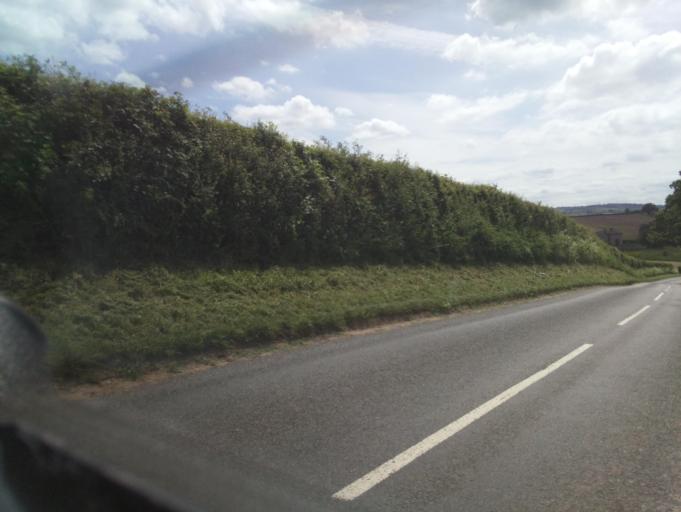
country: GB
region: England
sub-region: Herefordshire
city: Pencoyd
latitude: 51.9146
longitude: -2.6895
